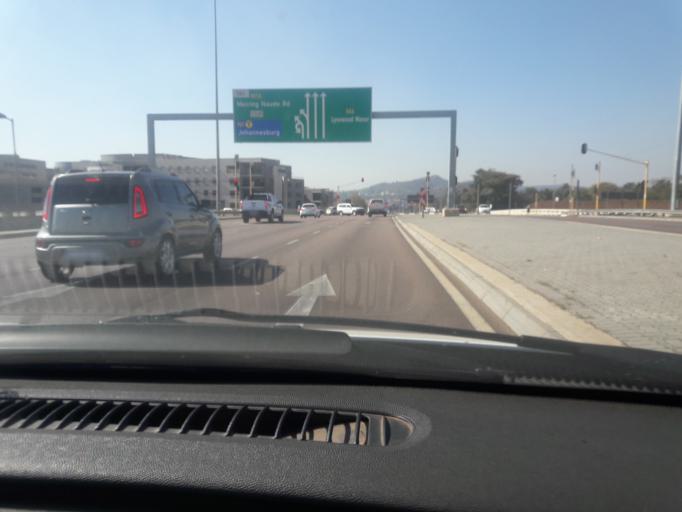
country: ZA
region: Gauteng
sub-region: City of Tshwane Metropolitan Municipality
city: Pretoria
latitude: -25.7659
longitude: 28.2750
